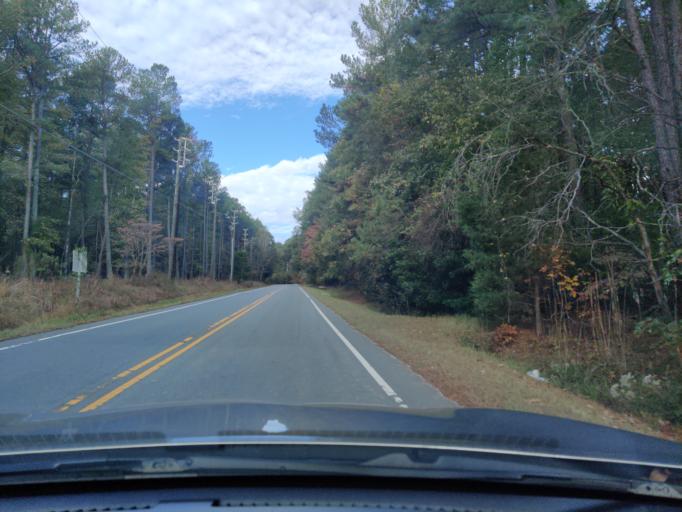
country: US
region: North Carolina
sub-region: Wake County
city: West Raleigh
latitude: 35.9197
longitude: -78.7168
